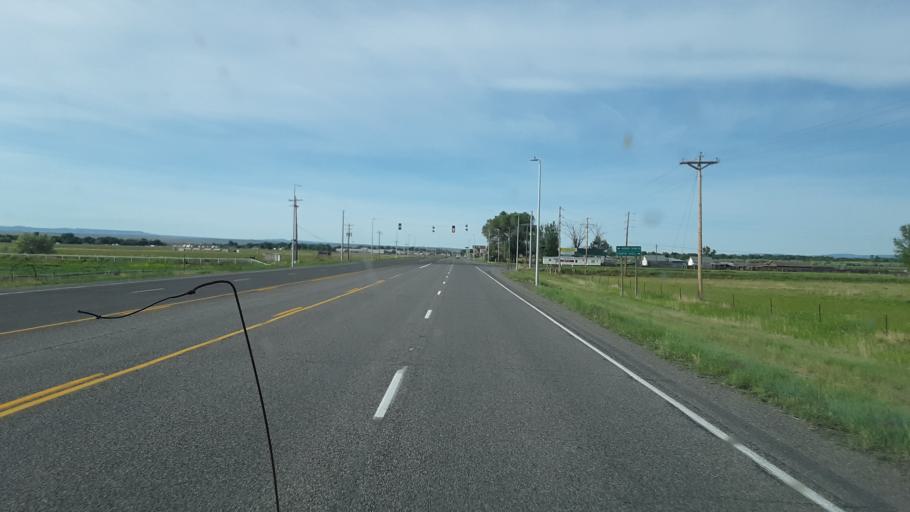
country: US
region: Wyoming
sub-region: Fremont County
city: Riverton
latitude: 43.0572
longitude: -108.3809
